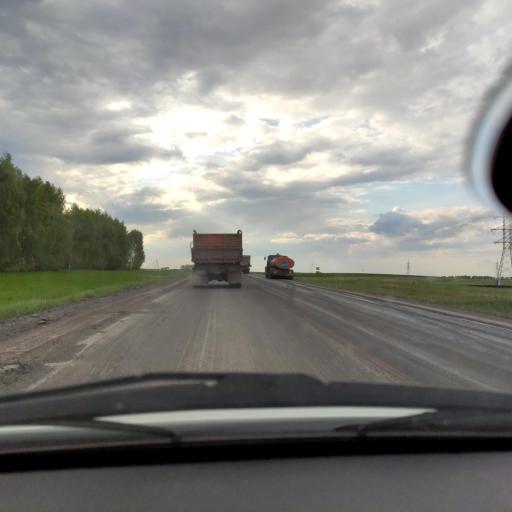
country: RU
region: Bashkortostan
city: Dyurtyuli
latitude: 55.3352
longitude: 54.9534
